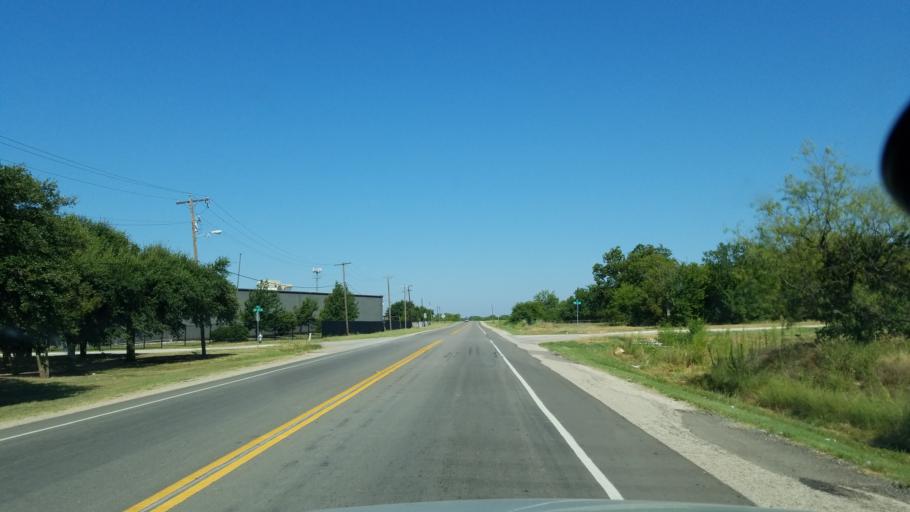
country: US
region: Texas
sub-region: Tarrant County
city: Mansfield
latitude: 32.5513
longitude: -97.1324
